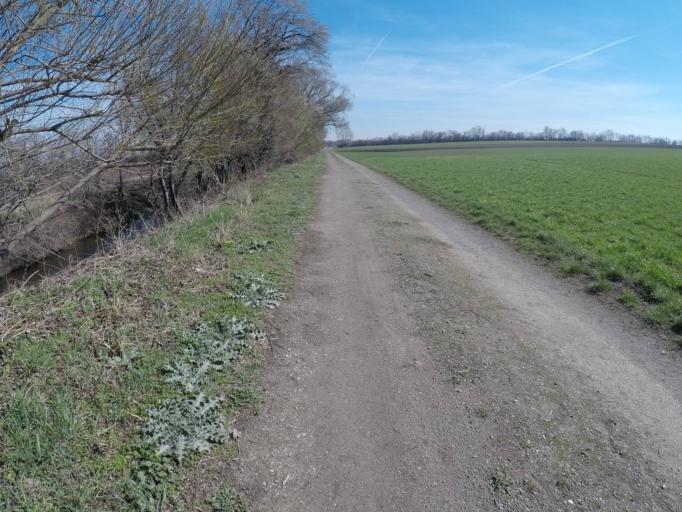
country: AT
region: Lower Austria
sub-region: Politischer Bezirk Modling
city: Biedermannsdorf
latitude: 48.0968
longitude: 16.3322
